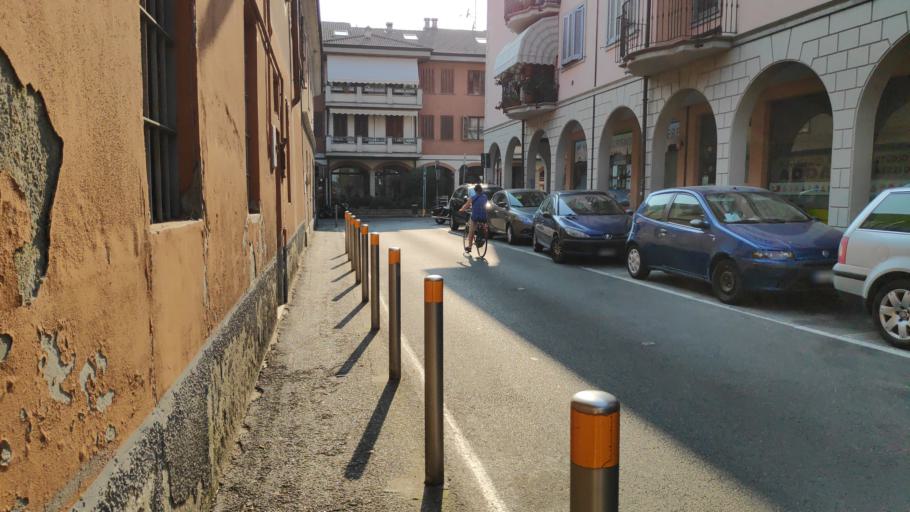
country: IT
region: Lombardy
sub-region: Citta metropolitana di Milano
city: Paullo
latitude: 45.4174
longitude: 9.4010
